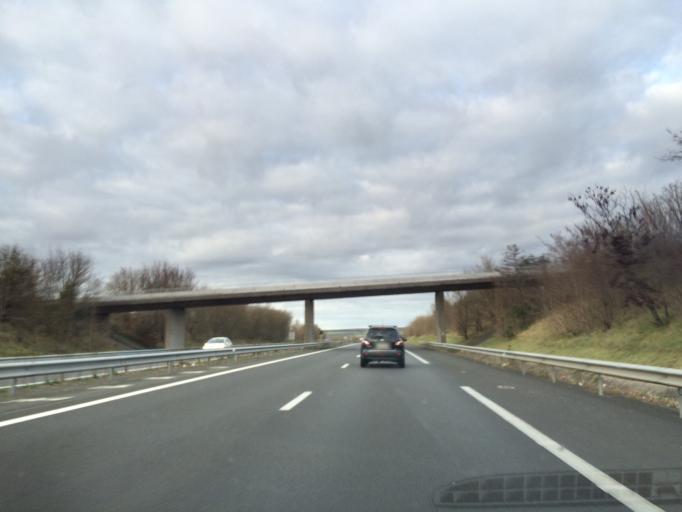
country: FR
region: Poitou-Charentes
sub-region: Departement de la Charente-Maritime
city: Saint-Jean-d'Angely
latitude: 46.0403
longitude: -0.5366
